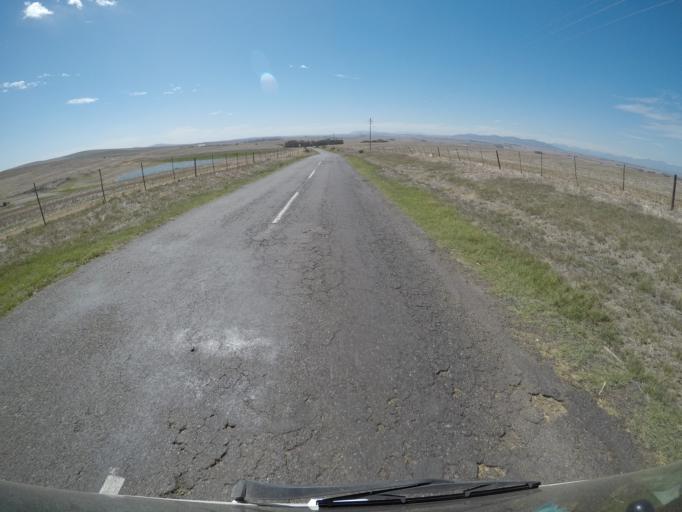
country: ZA
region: Western Cape
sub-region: City of Cape Town
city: Atlantis
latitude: -33.7068
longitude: 18.5853
